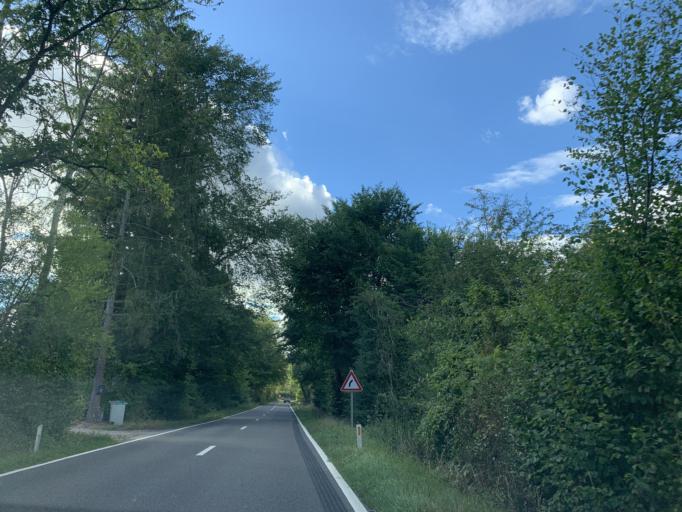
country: BE
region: Wallonia
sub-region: Province du Luxembourg
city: Tellin
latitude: 50.0956
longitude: 5.2707
